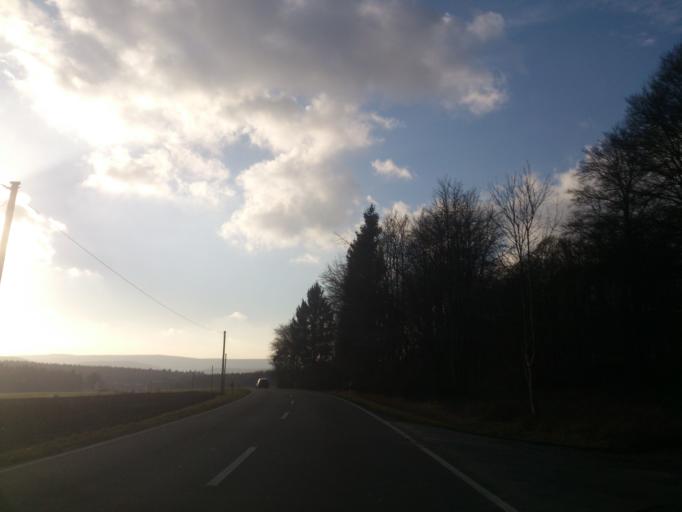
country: DE
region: North Rhine-Westphalia
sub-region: Regierungsbezirk Detmold
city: Nieheim
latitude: 51.7495
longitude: 9.0953
